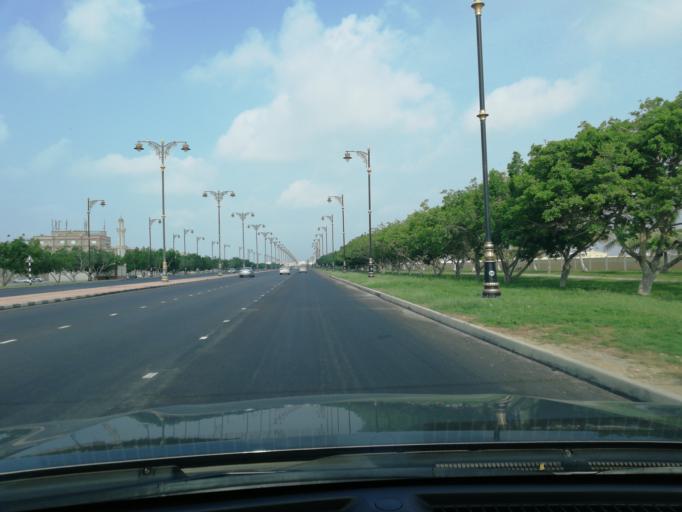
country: OM
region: Zufar
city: Salalah
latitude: 17.0235
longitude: 54.0832
